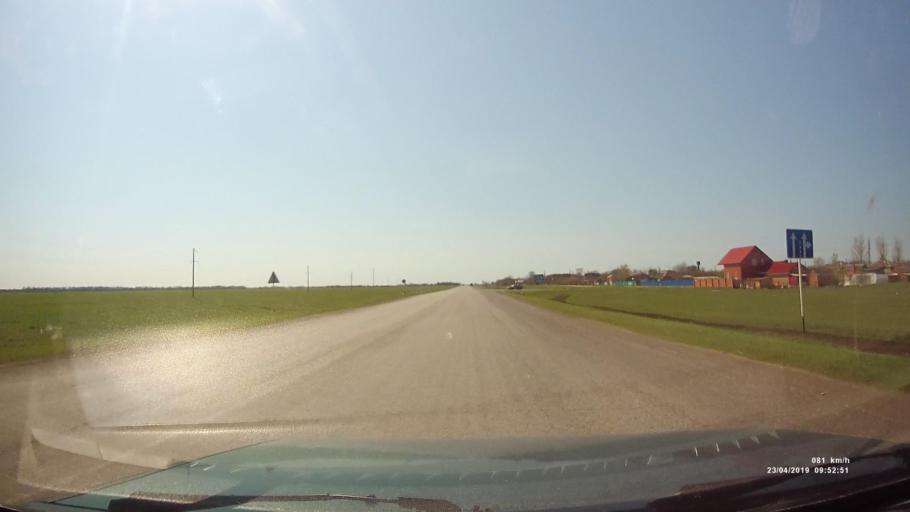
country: RU
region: Rostov
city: Orlovskiy
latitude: 46.8396
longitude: 42.0478
